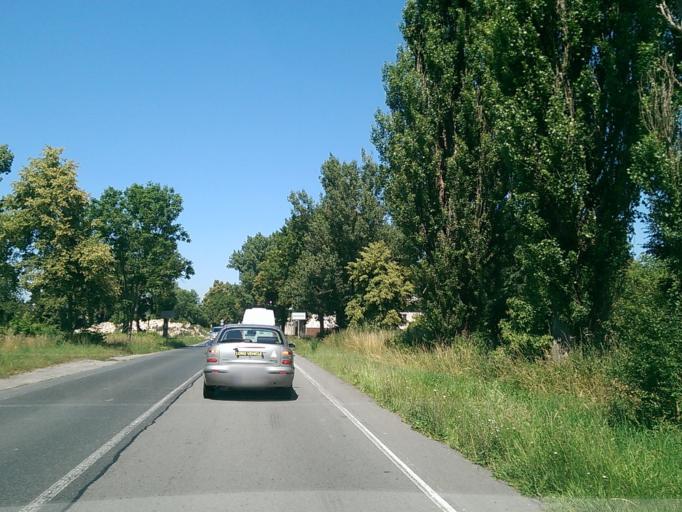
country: CZ
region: Central Bohemia
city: Benatky nad Jizerou
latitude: 50.3232
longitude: 14.8645
